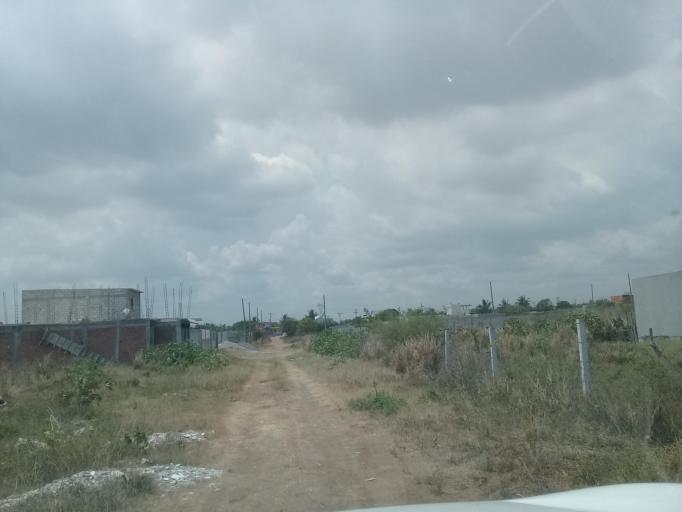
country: MX
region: Veracruz
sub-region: Veracruz
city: Las Amapolas
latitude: 19.1421
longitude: -96.2346
